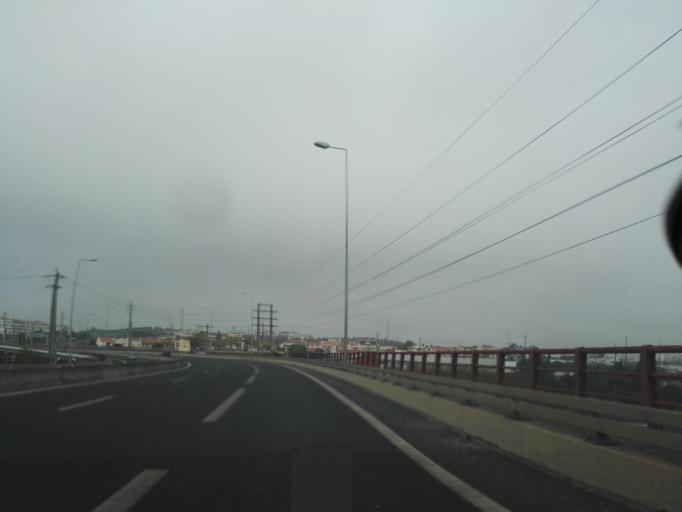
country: PT
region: Lisbon
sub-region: Loures
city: Santa Iria da Azoia
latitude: 38.8450
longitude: -9.0769
